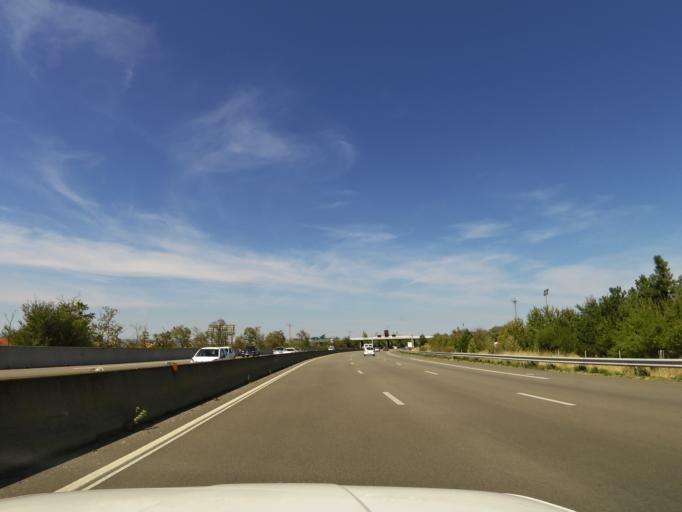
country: FR
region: Rhone-Alpes
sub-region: Departement de l'Isere
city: Chanas
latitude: 45.2841
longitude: 4.8220
